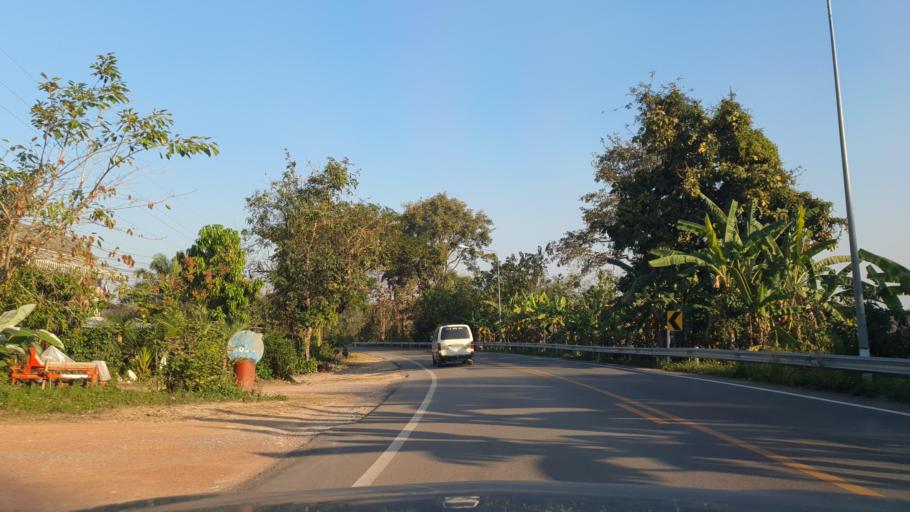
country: TH
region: Chiang Rai
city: Mae Lao
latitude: 19.8327
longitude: 99.6868
